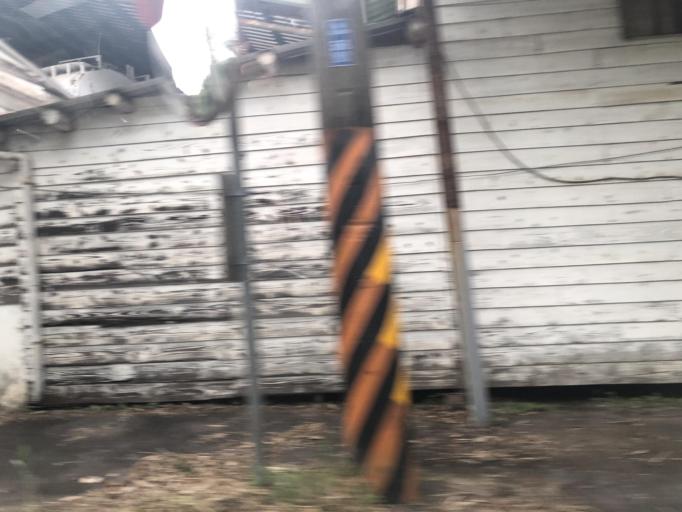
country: TW
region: Taiwan
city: Daxi
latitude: 24.9174
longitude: 121.3530
